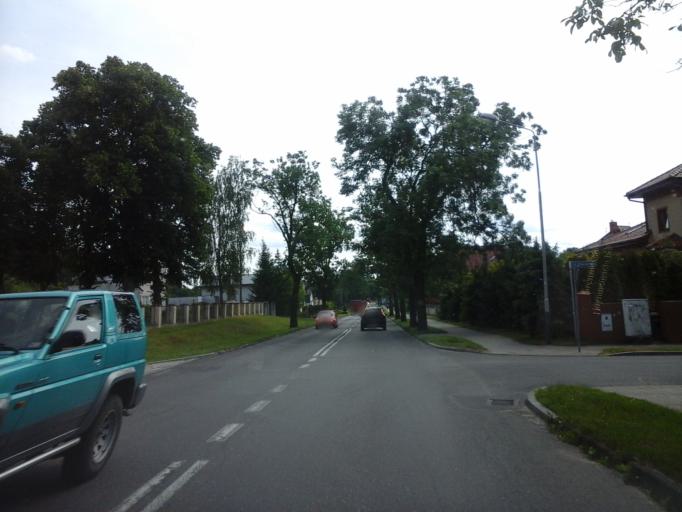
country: PL
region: West Pomeranian Voivodeship
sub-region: Powiat lobeski
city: Lobez
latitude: 53.6316
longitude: 15.6154
